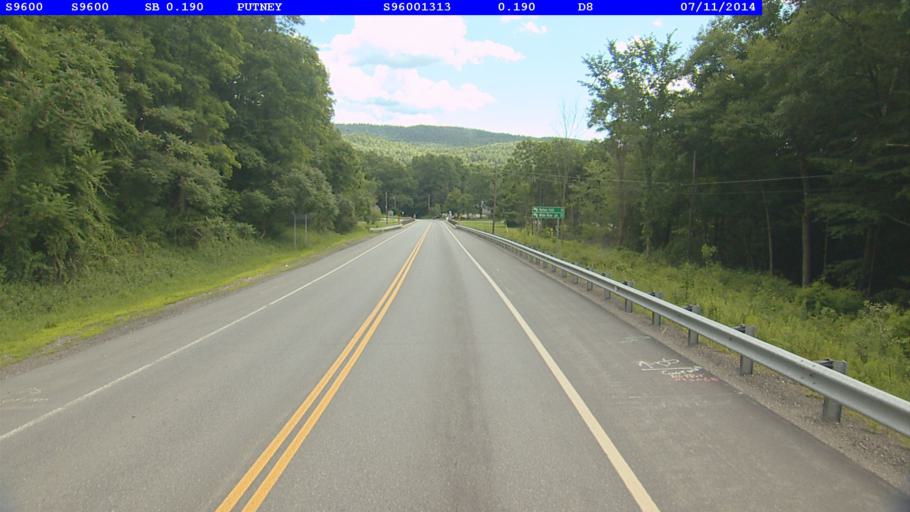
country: US
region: New Hampshire
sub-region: Cheshire County
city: Westmoreland
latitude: 42.9664
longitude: -72.5219
